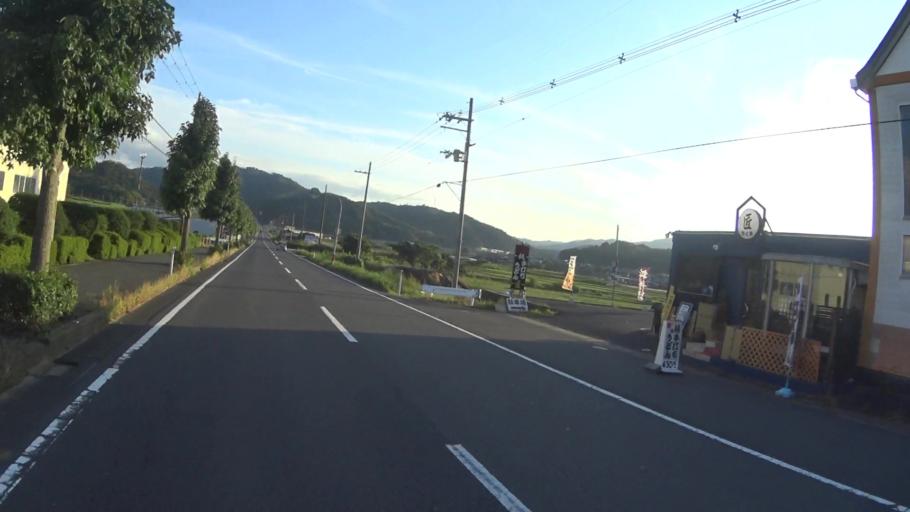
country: JP
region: Kyoto
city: Miyazu
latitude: 35.5763
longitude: 135.0987
